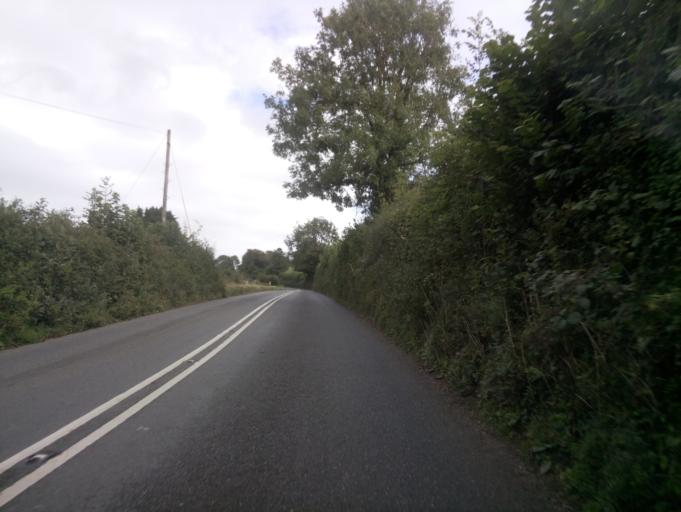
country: GB
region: England
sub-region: Devon
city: Modbury
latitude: 50.3426
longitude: -3.8786
